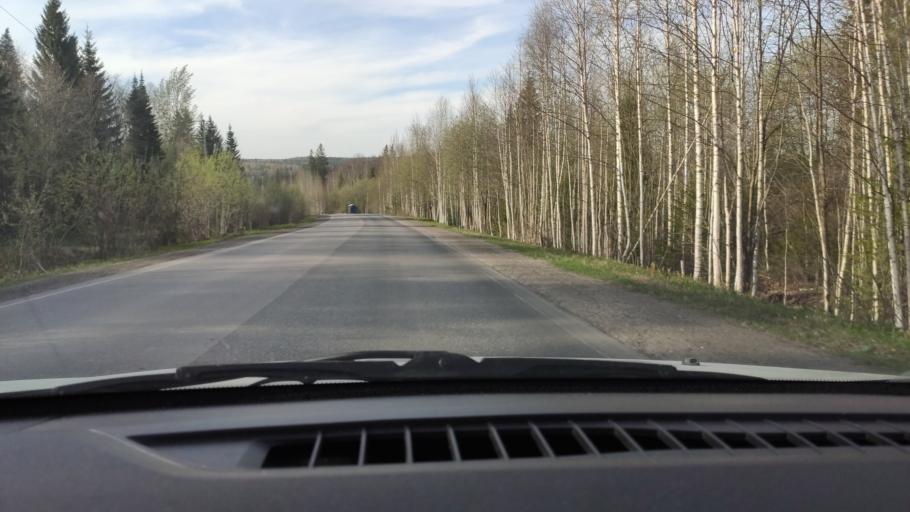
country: RU
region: Perm
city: Novyye Lyady
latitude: 57.9525
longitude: 56.5688
